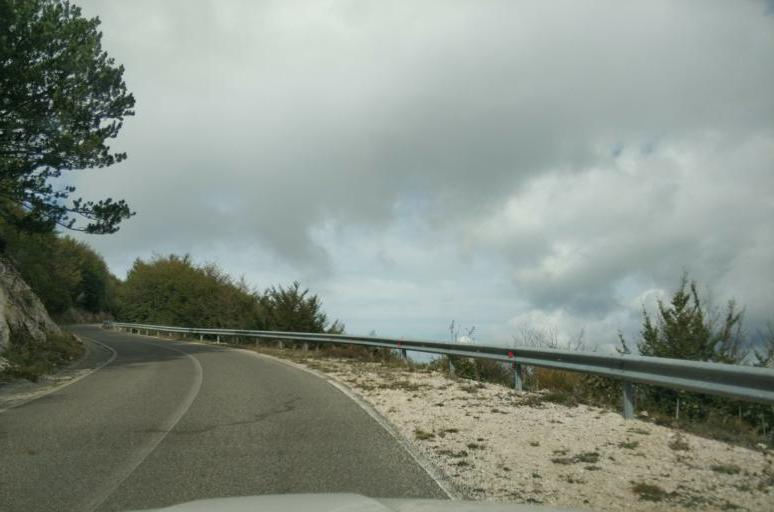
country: AL
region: Durres
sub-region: Rrethi i Krujes
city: Kruje
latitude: 41.5184
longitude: 19.8056
